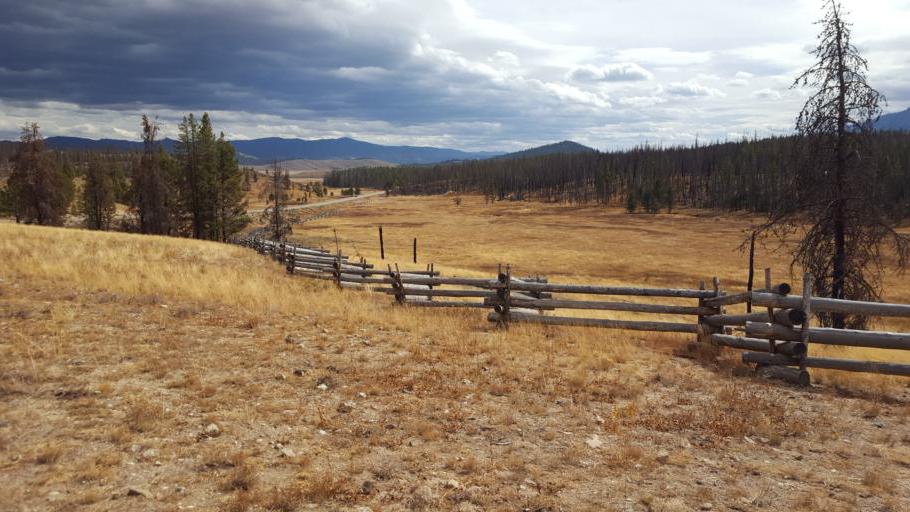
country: US
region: Idaho
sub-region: Custer County
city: Challis
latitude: 44.2825
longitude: -115.0275
